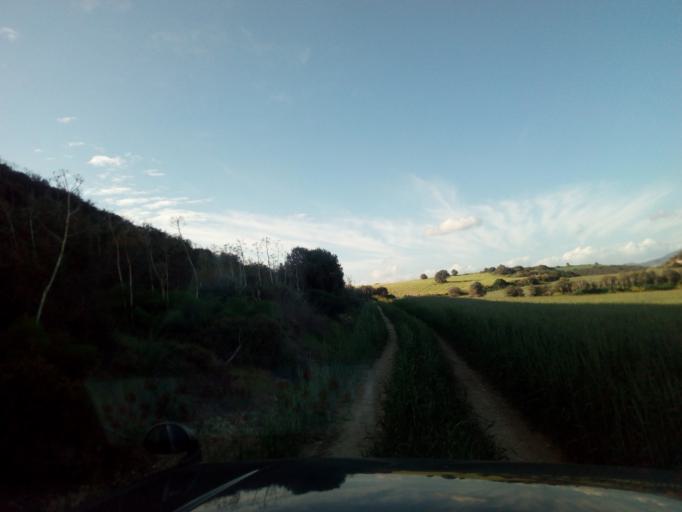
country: CY
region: Larnaka
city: Kofinou
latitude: 34.7997
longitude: 33.4228
